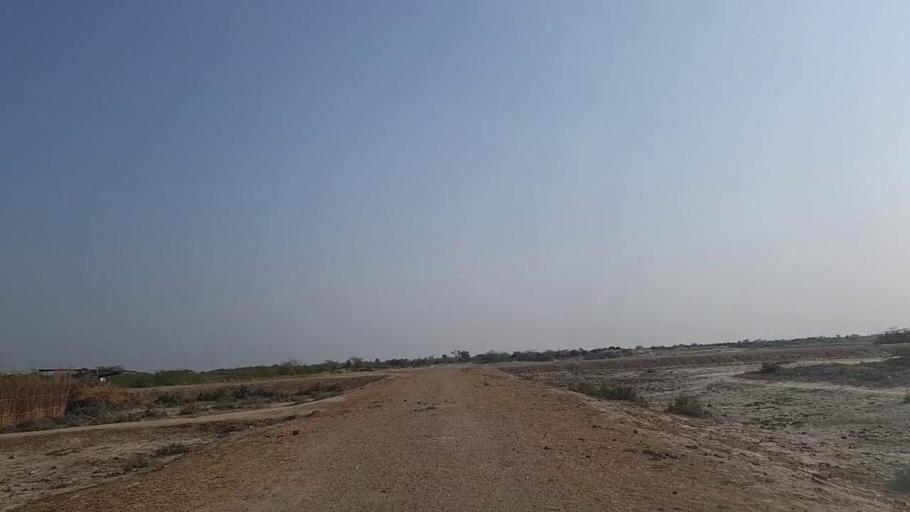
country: PK
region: Sindh
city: Dhoro Naro
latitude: 25.4837
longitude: 69.5290
